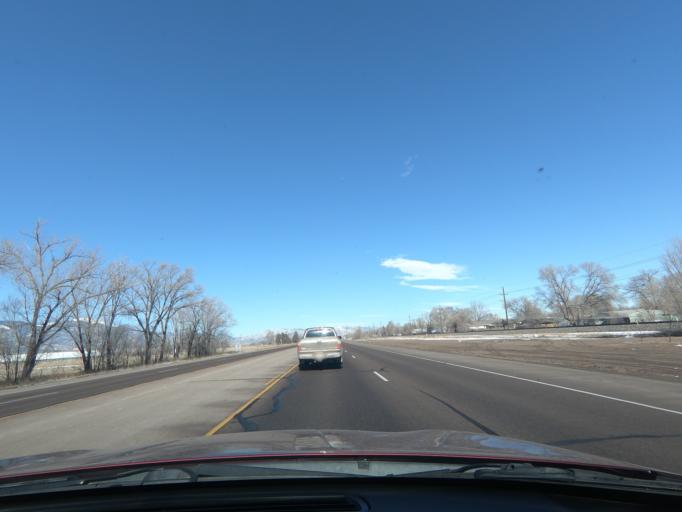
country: US
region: Colorado
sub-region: El Paso County
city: Stratmoor
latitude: 38.7579
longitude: -104.7503
